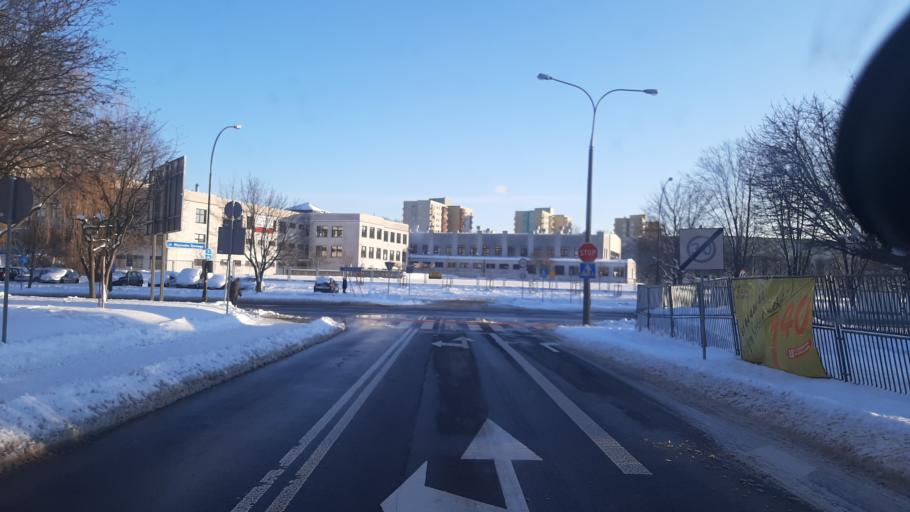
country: PL
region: Lublin Voivodeship
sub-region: Powiat lubelski
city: Lublin
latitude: 51.2685
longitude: 22.5516
